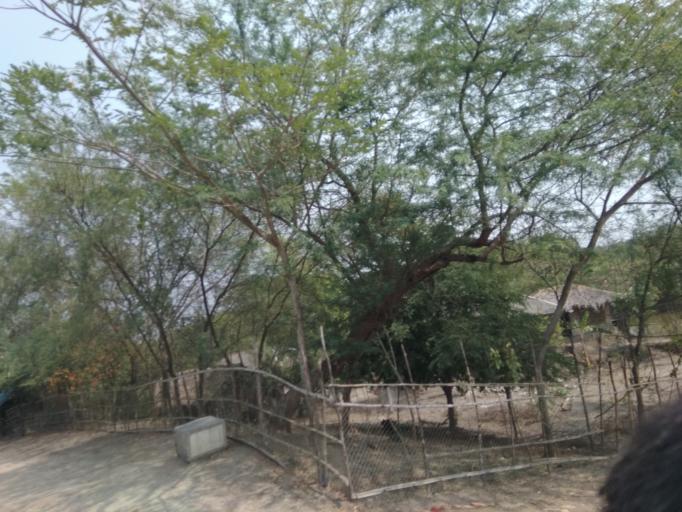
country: IN
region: West Bengal
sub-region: North 24 Parganas
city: Gosaba
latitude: 22.2563
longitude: 89.2519
